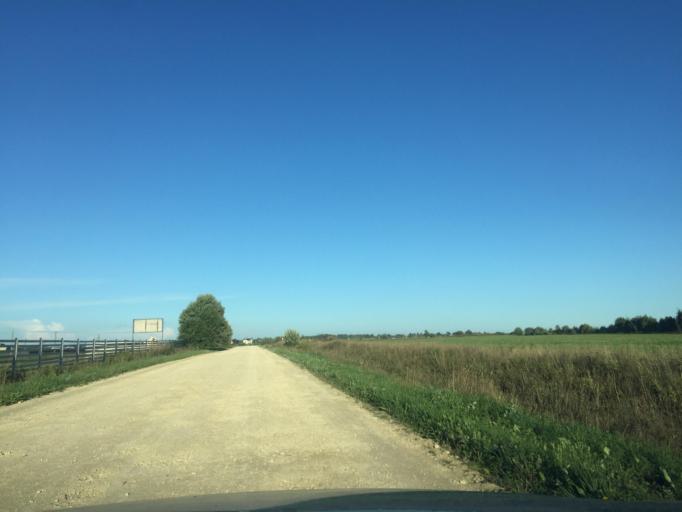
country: RU
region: Leningrad
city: Rozhdestveno
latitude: 59.3326
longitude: 30.0058
